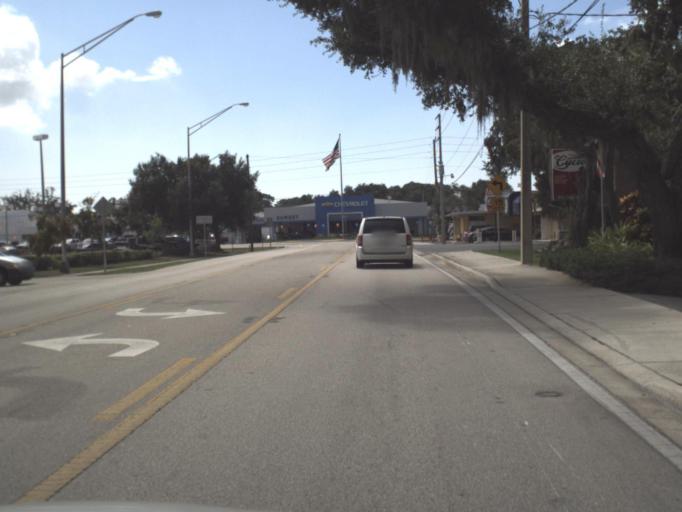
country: US
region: Florida
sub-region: Sarasota County
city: South Sarasota
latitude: 27.3002
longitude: -82.5337
